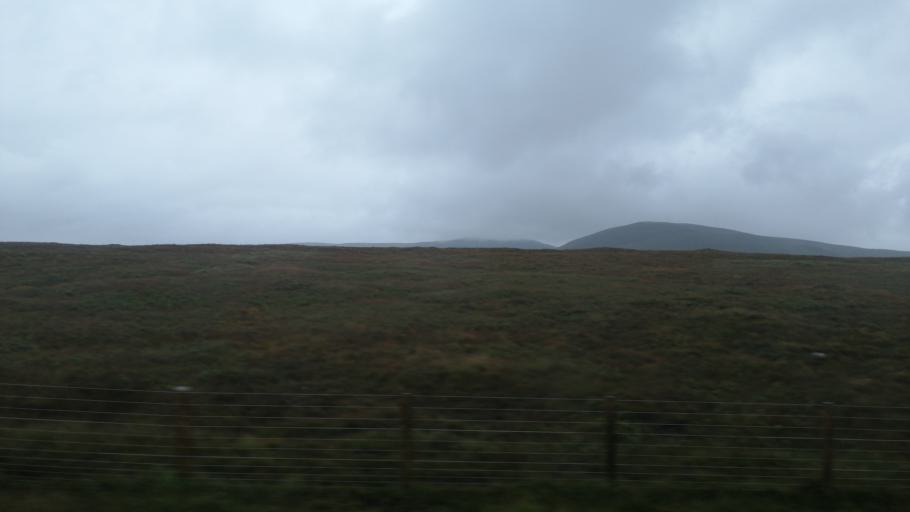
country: GB
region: Scotland
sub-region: Highland
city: Brora
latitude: 58.3557
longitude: -3.9082
